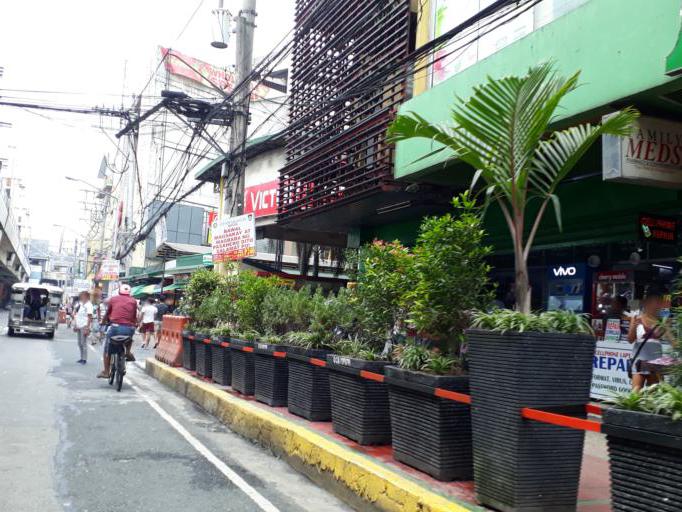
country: PH
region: Metro Manila
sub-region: Caloocan City
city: Niugan
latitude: 14.6562
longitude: 120.9838
